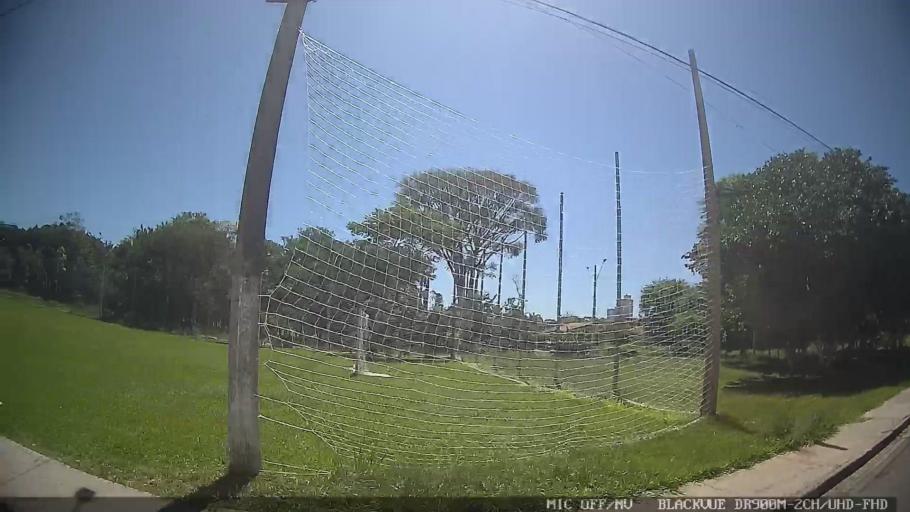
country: BR
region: Sao Paulo
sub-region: Atibaia
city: Atibaia
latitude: -23.1112
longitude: -46.5649
